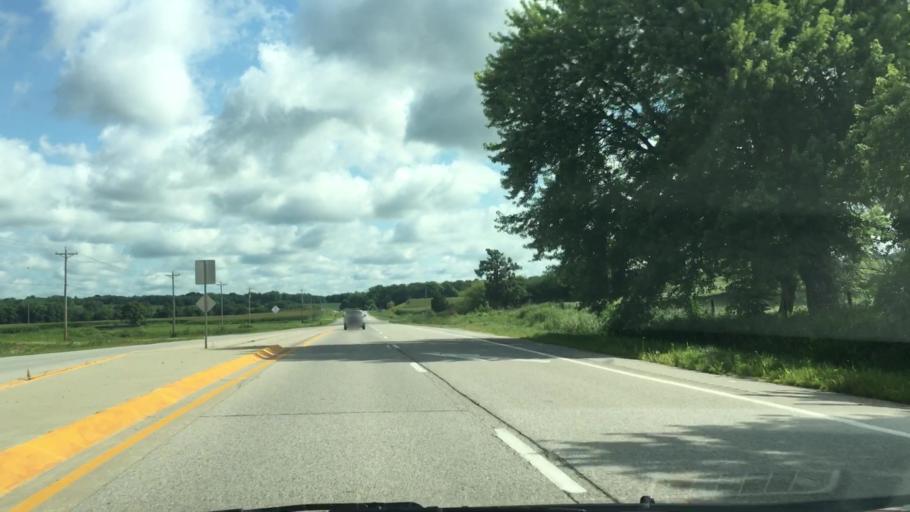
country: US
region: Iowa
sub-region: Johnson County
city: Iowa City
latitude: 41.6937
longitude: -91.4947
